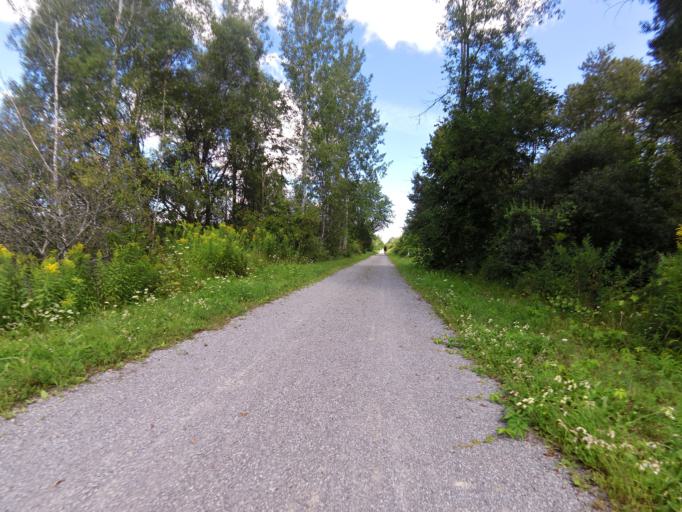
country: CA
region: Ontario
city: Ottawa
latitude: 45.2903
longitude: -75.6269
